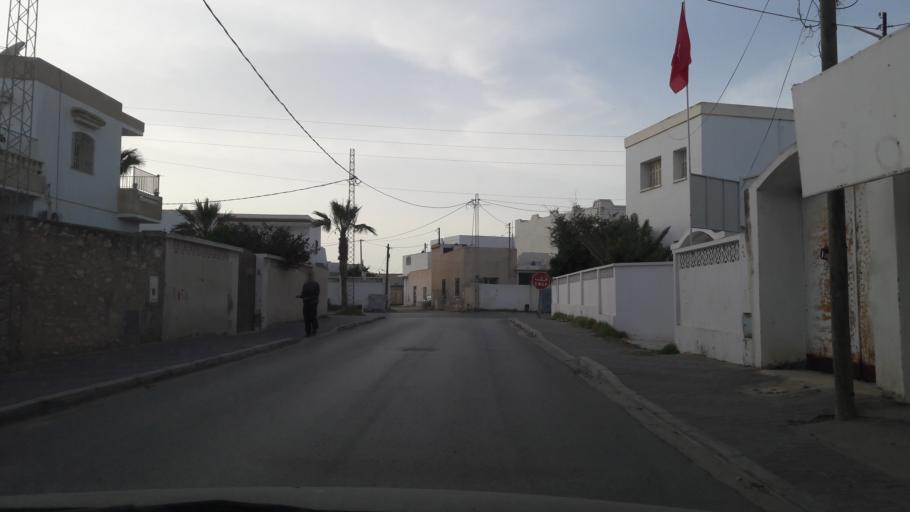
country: TN
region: Safaqis
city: Al Qarmadah
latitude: 34.8009
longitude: 10.7590
